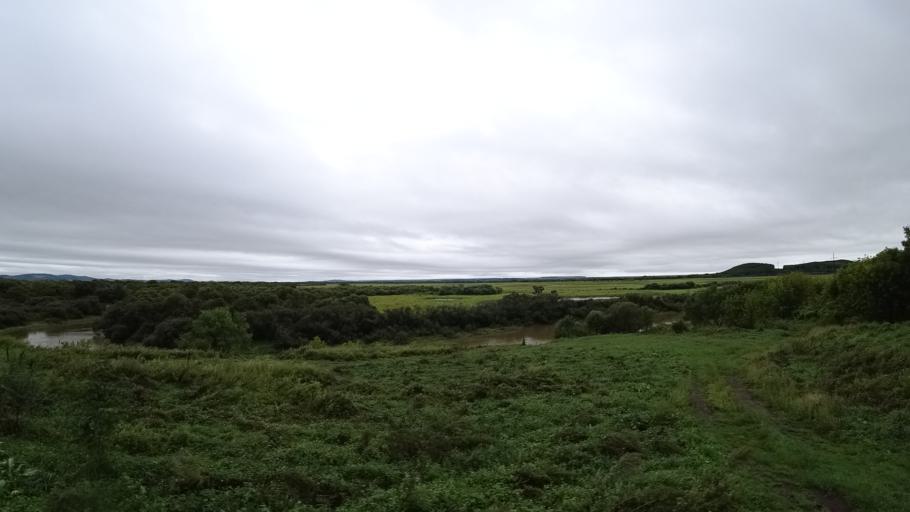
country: RU
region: Primorskiy
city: Monastyrishche
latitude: 44.2618
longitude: 132.4055
